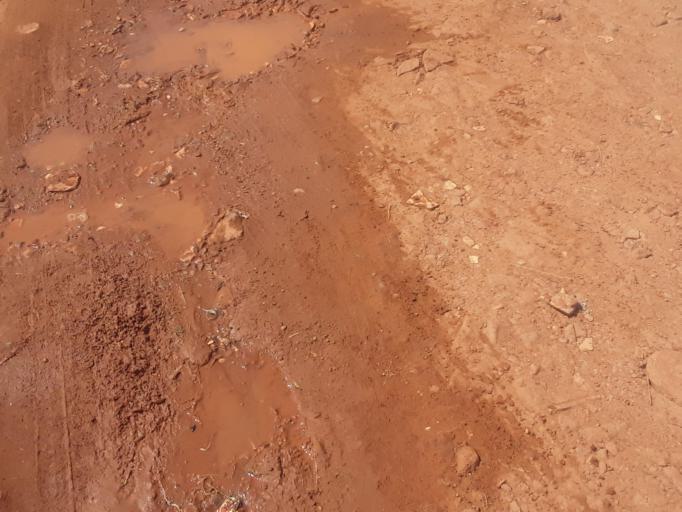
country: ZM
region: Lusaka
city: Lusaka
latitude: -15.3573
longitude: 28.2827
